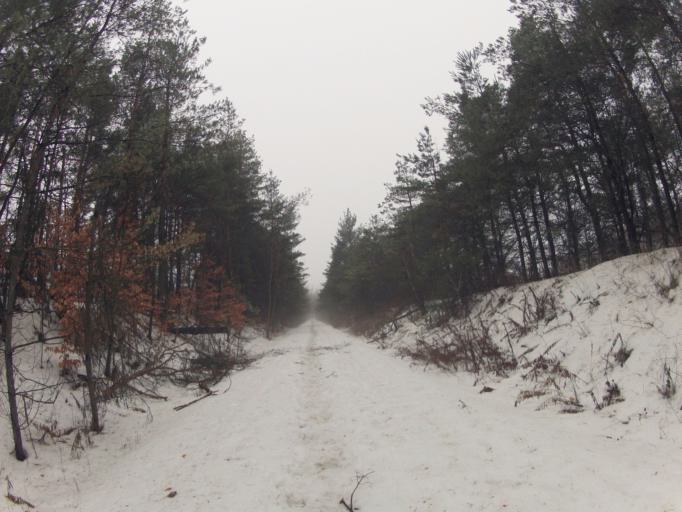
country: CA
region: Ontario
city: Brampton
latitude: 43.8397
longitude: -79.8885
